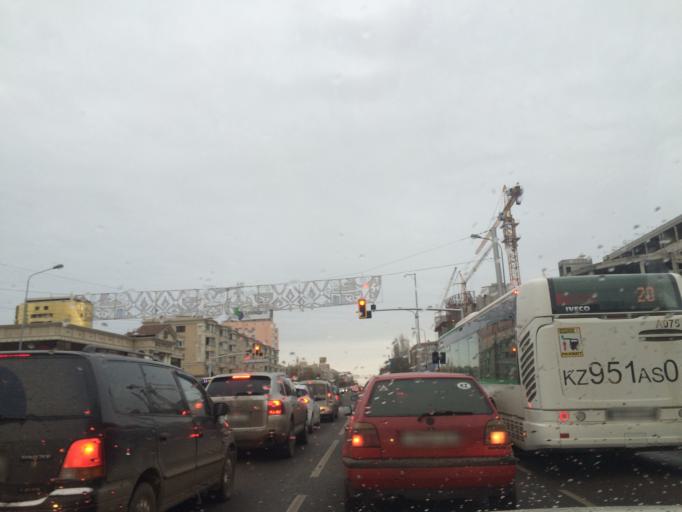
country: KZ
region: Astana Qalasy
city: Astana
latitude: 51.1623
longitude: 71.4285
